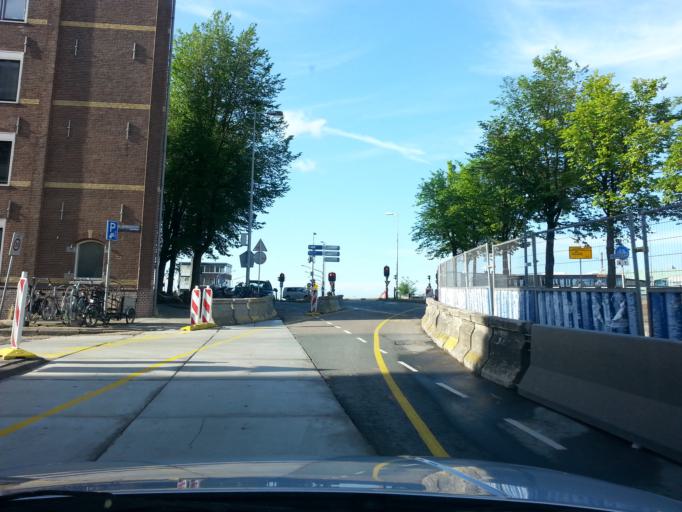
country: NL
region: North Holland
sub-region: Gemeente Amsterdam
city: Amsterdam
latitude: 52.3900
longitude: 4.8848
